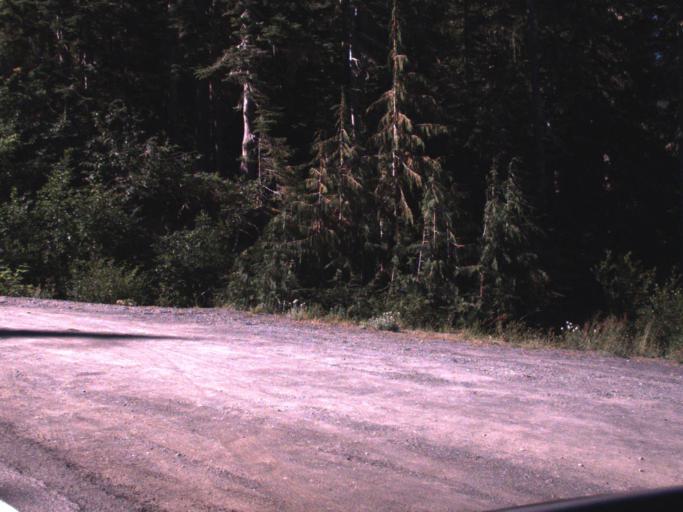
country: US
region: Washington
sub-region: King County
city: Enumclaw
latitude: 46.8812
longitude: -121.5398
